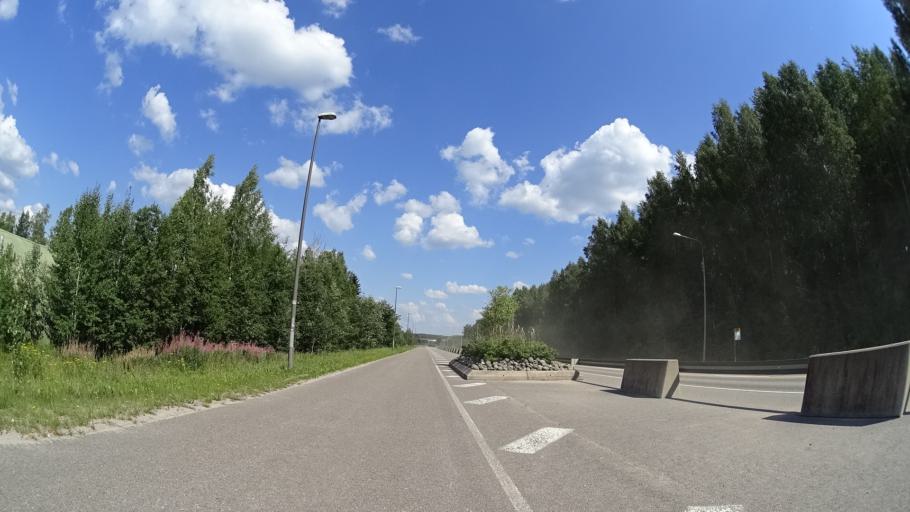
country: FI
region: Uusimaa
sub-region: Helsinki
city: Vantaa
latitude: 60.3258
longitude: 24.9192
